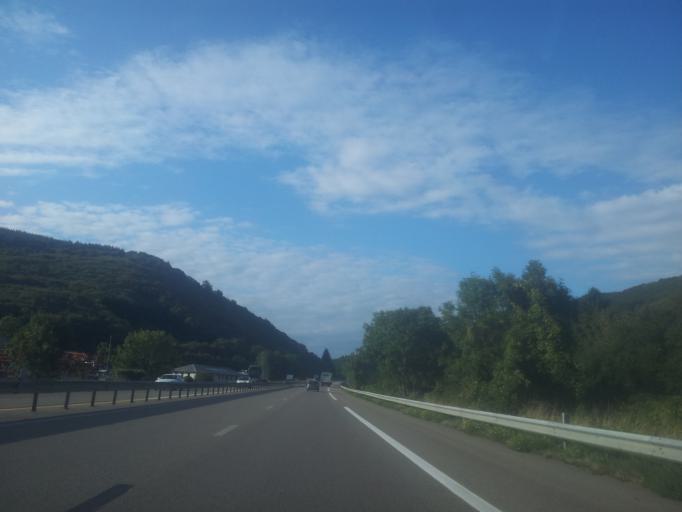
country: FR
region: Rhone-Alpes
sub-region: Departement de l'Isere
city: Colombe
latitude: 45.4014
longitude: 5.4647
